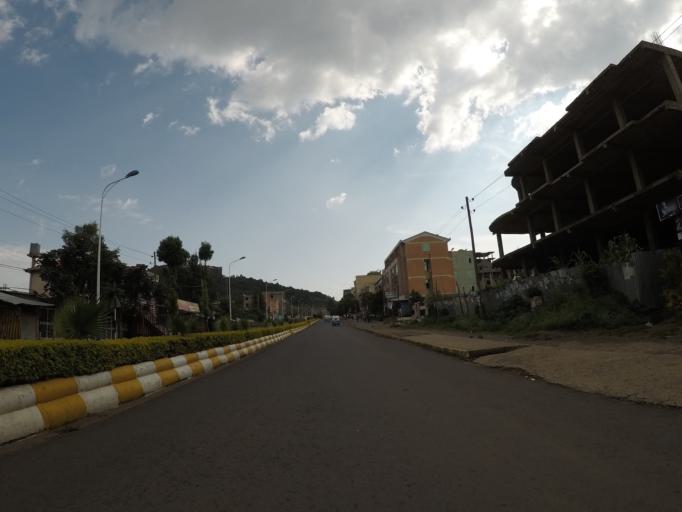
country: ET
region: Amhara
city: Gondar
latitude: 12.5950
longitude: 37.4481
